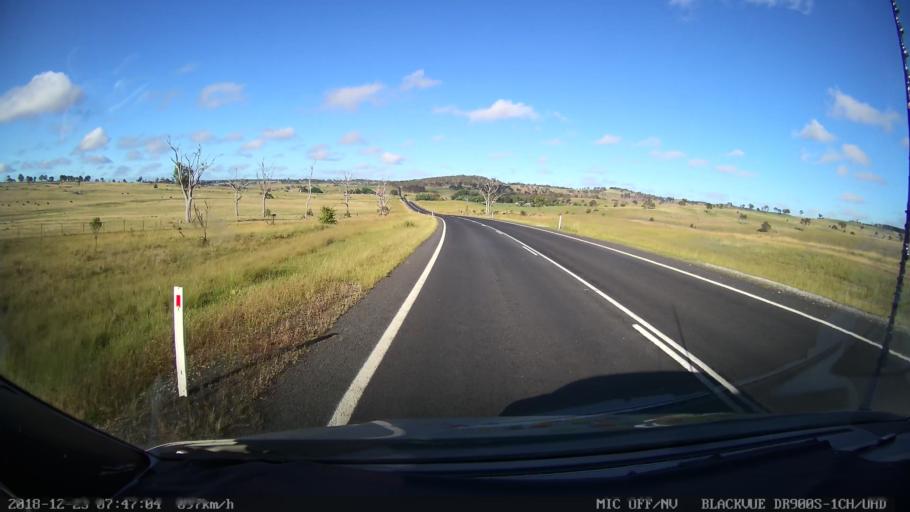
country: AU
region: New South Wales
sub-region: Armidale Dumaresq
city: Enmore
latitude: -30.5256
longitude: 151.9078
